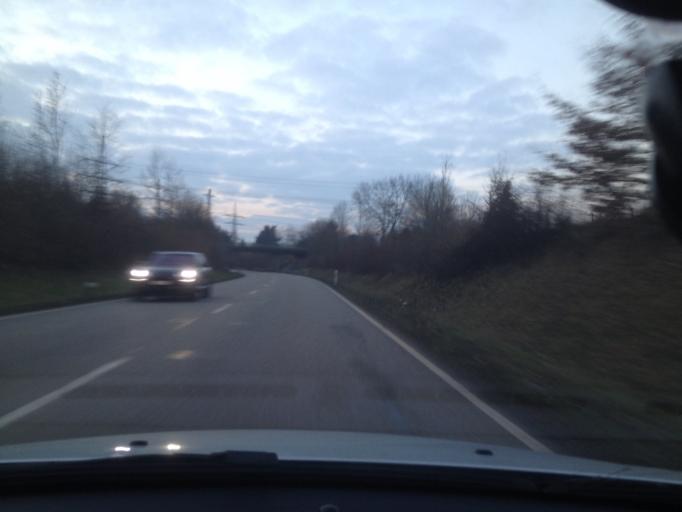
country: DE
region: Baden-Wuerttemberg
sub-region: Karlsruhe Region
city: Ettlingen
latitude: 48.9565
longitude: 8.4105
